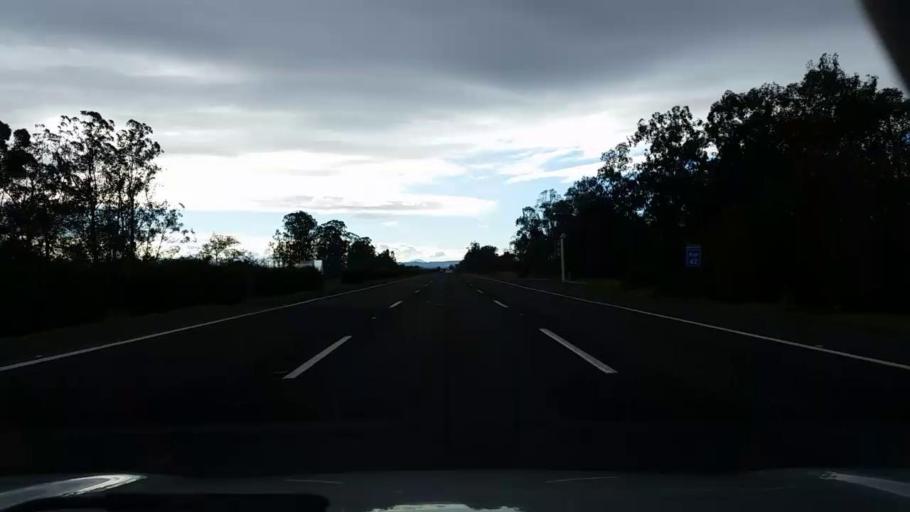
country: BR
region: Rio Grande do Sul
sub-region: Taquara
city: Taquara
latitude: -29.8890
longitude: -50.6789
